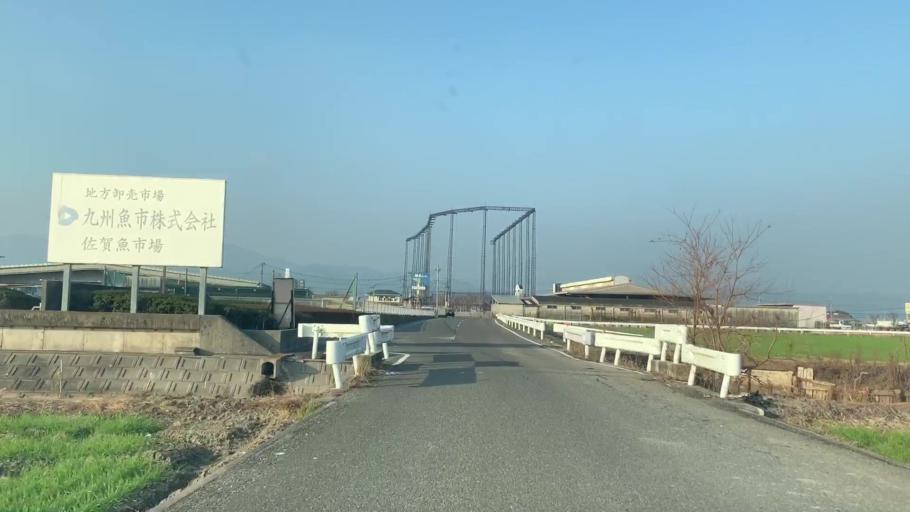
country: JP
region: Saga Prefecture
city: Saga-shi
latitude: 33.2627
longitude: 130.2480
